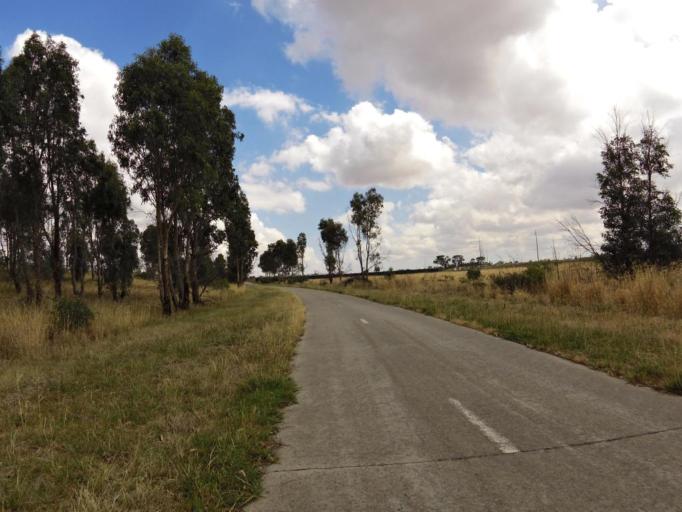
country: AU
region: Victoria
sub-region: Whittlesea
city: Epping
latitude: -37.6236
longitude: 144.9938
